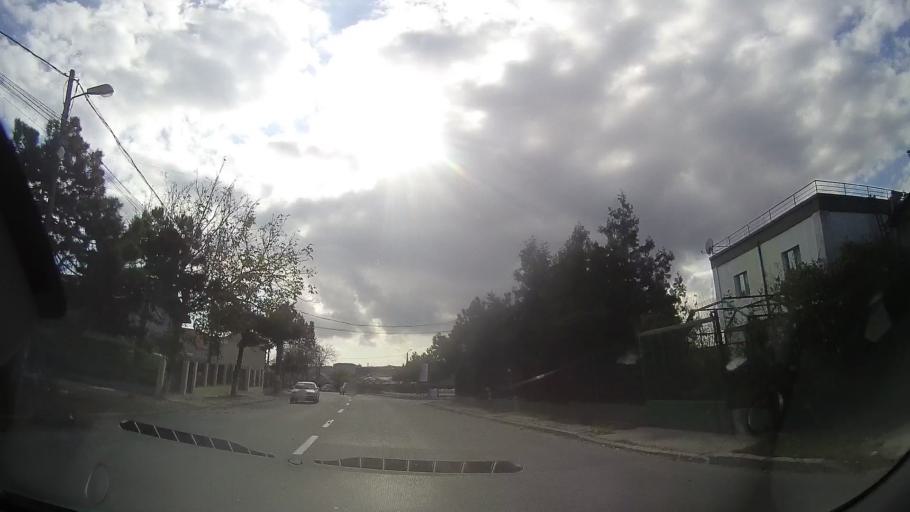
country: RO
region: Constanta
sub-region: Oras Techirghiol
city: Techirghiol
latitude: 44.0597
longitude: 28.5993
